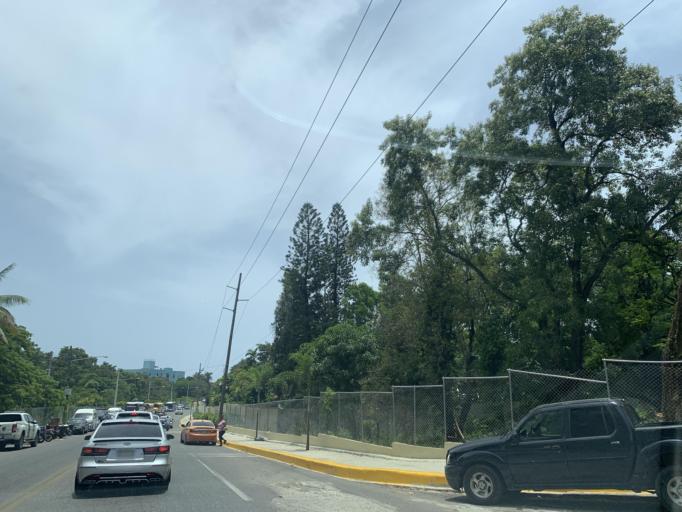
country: DO
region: Puerto Plata
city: Cabarete
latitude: 19.7586
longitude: -70.5154
